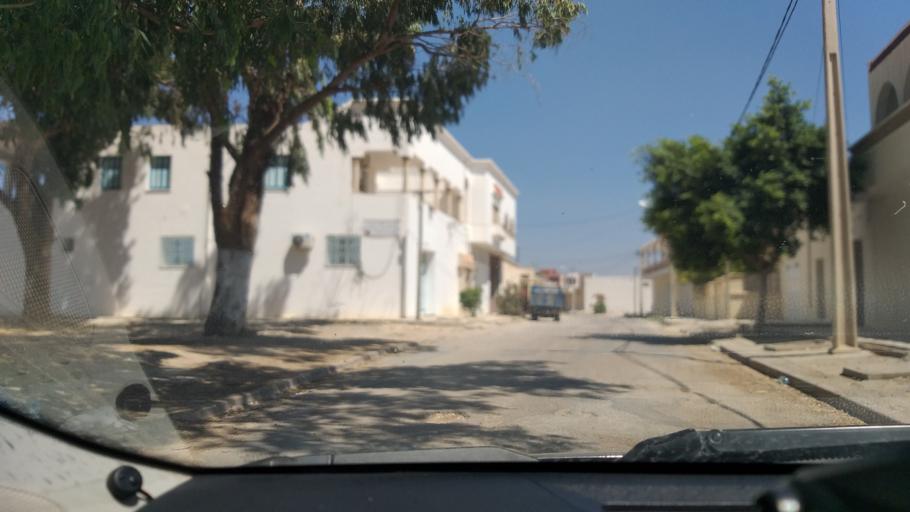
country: TN
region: Al Mahdiyah
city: El Jem
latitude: 35.2933
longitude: 10.7120
